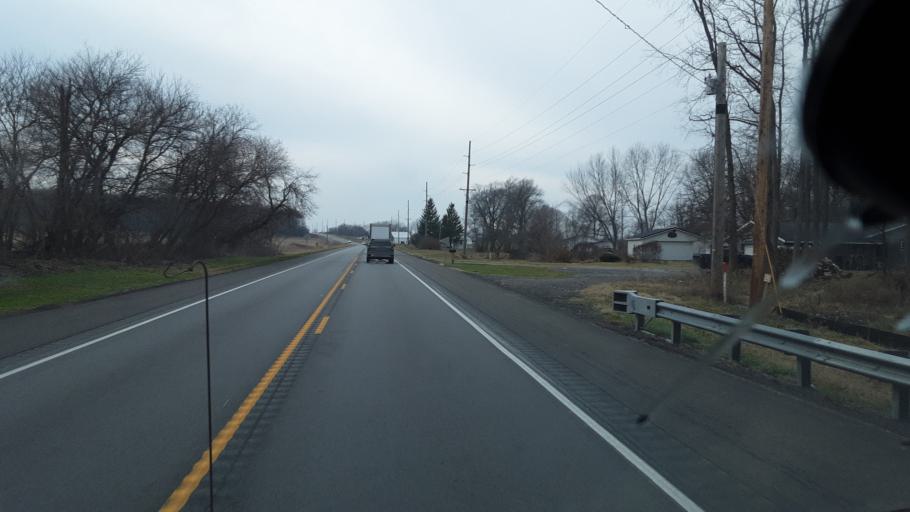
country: US
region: Indiana
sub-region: LaGrange County
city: Lagrange
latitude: 41.6413
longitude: -85.2549
